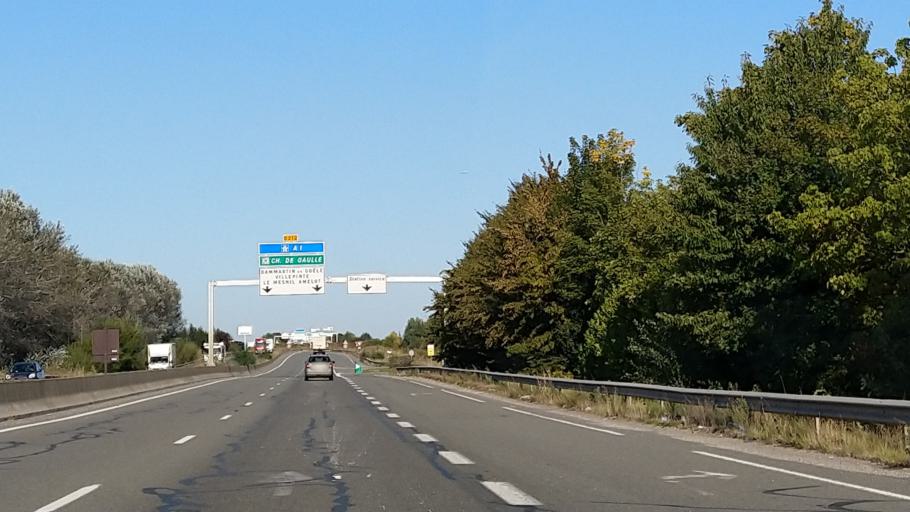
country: FR
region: Ile-de-France
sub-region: Departement de Seine-et-Marne
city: Mitry-Mory
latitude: 48.9937
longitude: 2.6531
